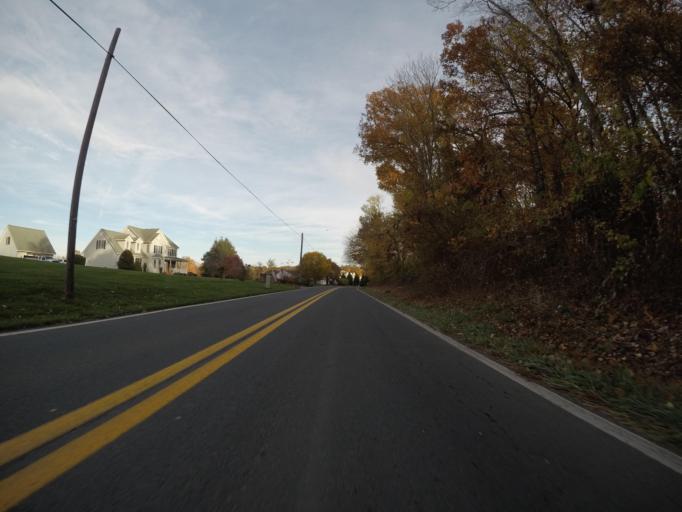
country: US
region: Maryland
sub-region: Carroll County
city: Hampstead
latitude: 39.5625
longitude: -76.8519
